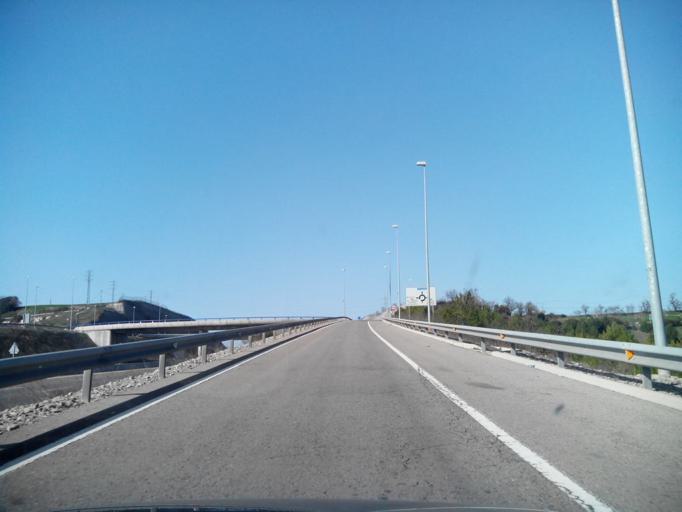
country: ES
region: Catalonia
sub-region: Provincia de Lleida
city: Sant Guim de Freixenet
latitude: 41.6225
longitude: 1.4105
